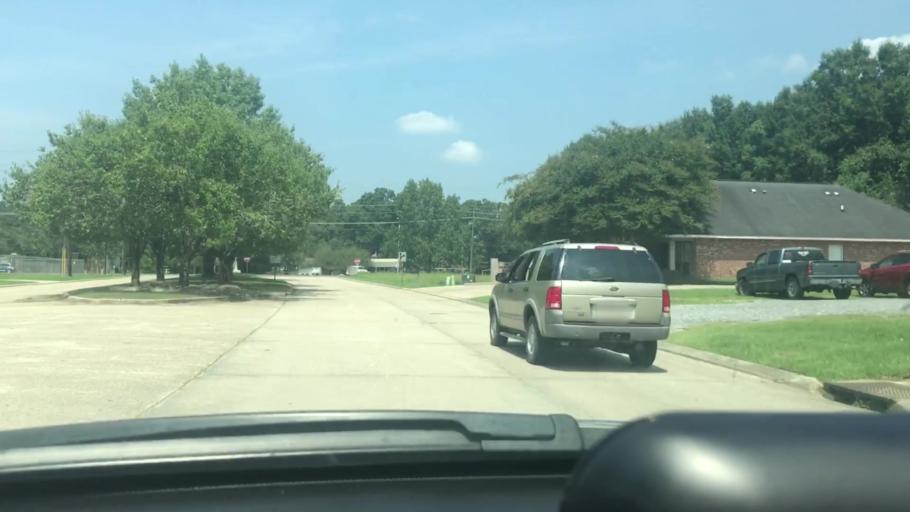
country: US
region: Louisiana
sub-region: Livingston Parish
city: Denham Springs
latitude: 30.4696
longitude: -90.9644
